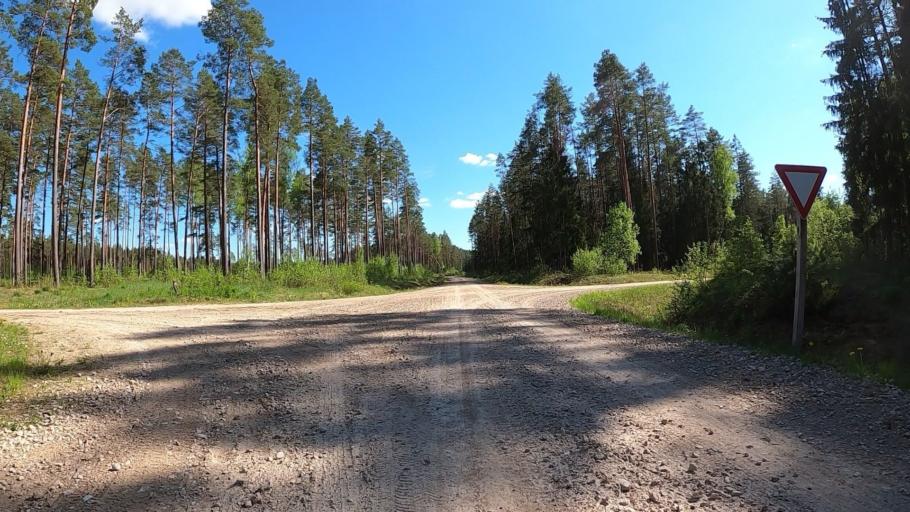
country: LV
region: Baldone
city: Baldone
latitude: 56.7757
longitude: 24.3744
